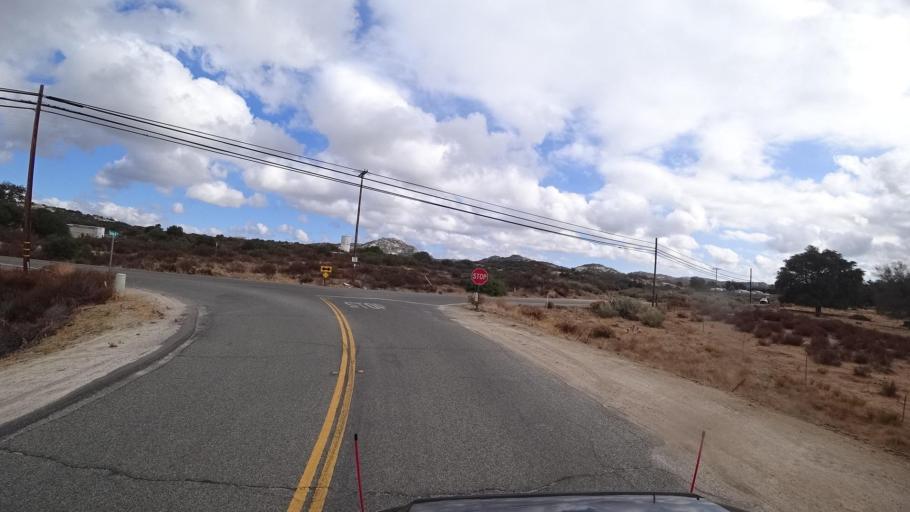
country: US
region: California
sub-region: San Diego County
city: Campo
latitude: 32.6300
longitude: -116.4580
